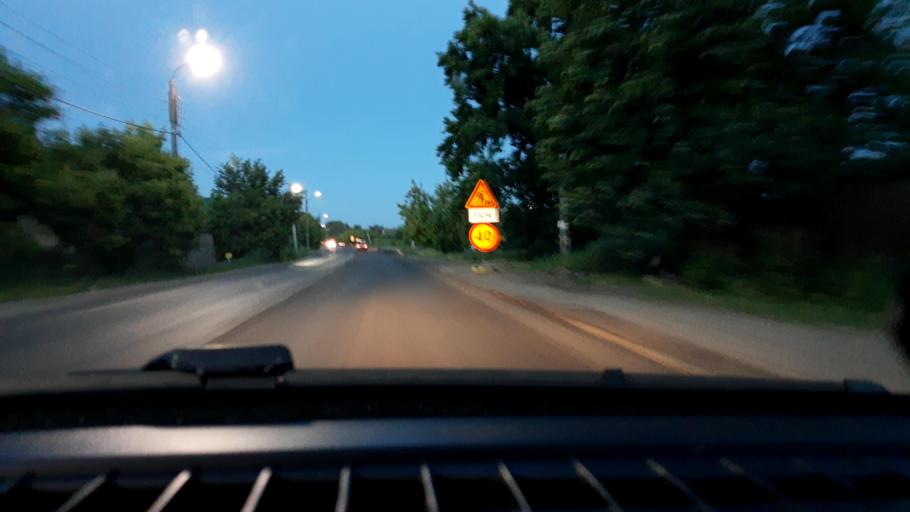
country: RU
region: Nizjnij Novgorod
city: Gidrotorf
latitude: 56.5358
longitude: 43.5382
